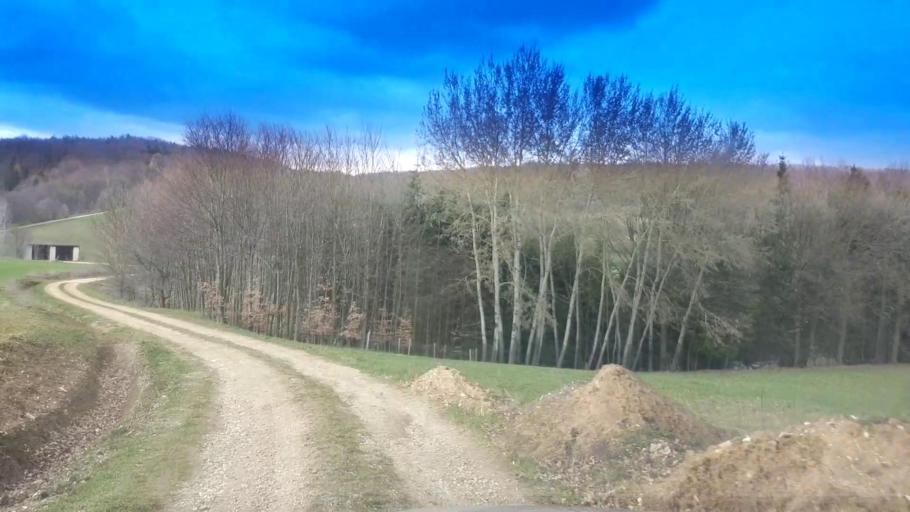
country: DE
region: Bavaria
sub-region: Upper Franconia
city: Schesslitz
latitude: 50.0077
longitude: 11.0377
